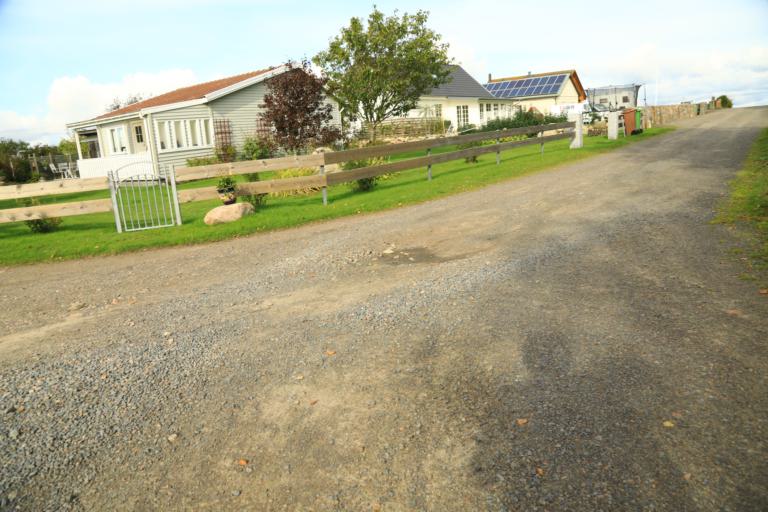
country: SE
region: Halland
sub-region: Varbergs Kommun
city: Tvaaker
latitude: 57.0213
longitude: 12.3385
